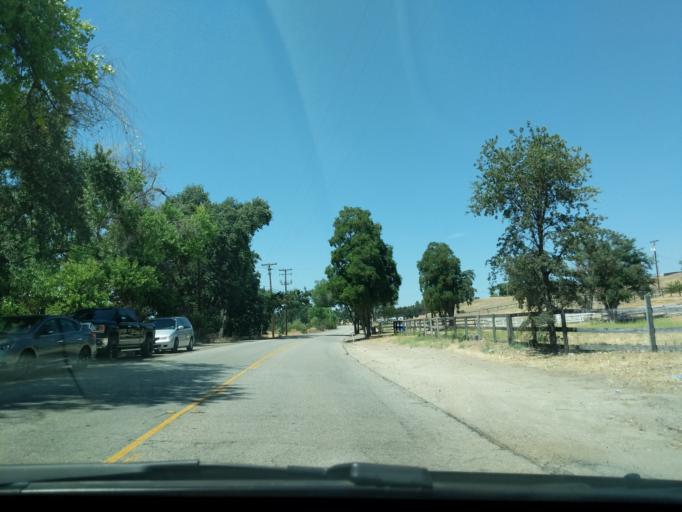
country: US
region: California
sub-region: San Luis Obispo County
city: Paso Robles
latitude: 35.6493
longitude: -120.6410
